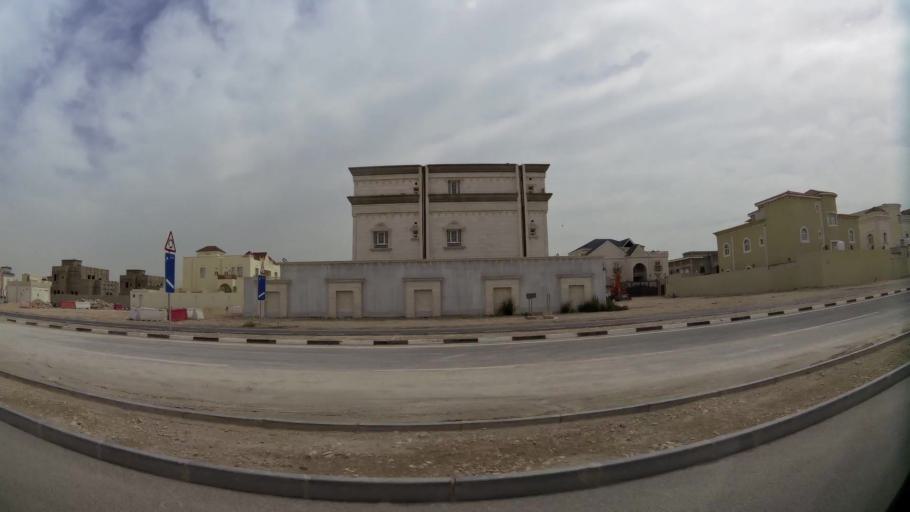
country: QA
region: Al Wakrah
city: Al Wukayr
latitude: 25.2074
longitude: 51.4724
